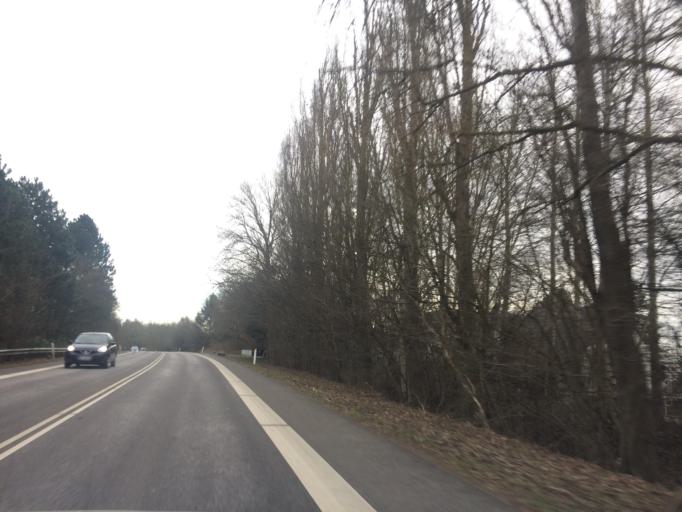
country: DK
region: Capital Region
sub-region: Fredensborg Kommune
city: Kokkedal
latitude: 55.9245
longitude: 12.4448
